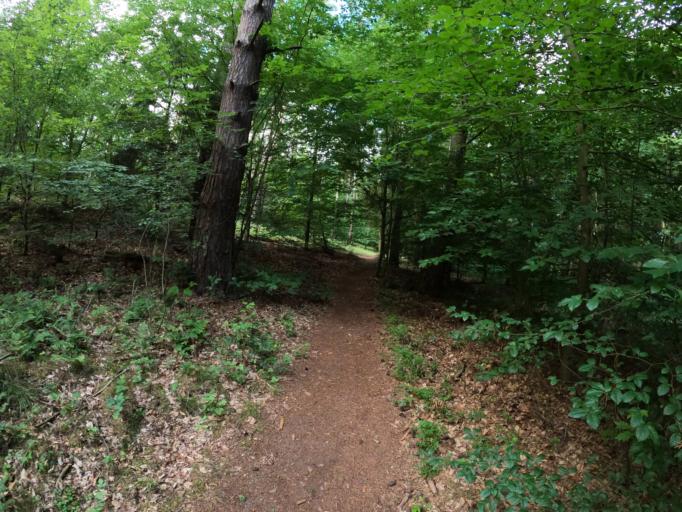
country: DE
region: Brandenburg
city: Angermunde
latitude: 53.0281
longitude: 13.9309
